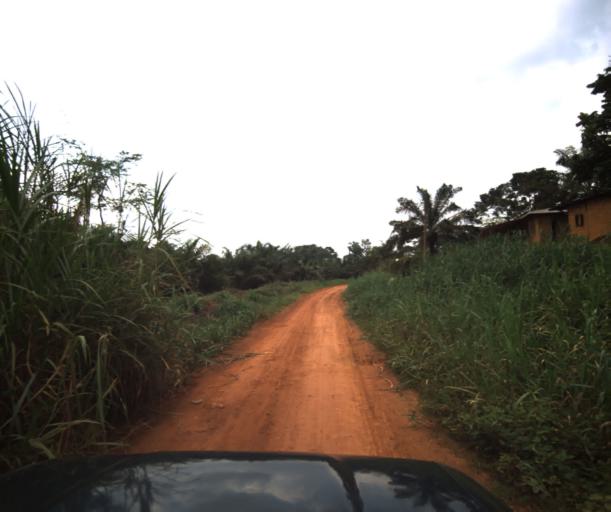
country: CM
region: Centre
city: Akono
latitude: 3.5963
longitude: 11.1689
